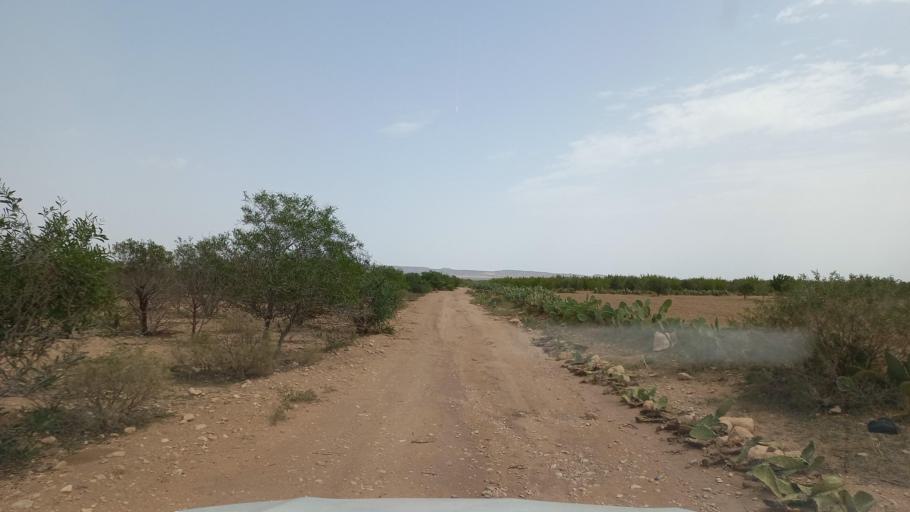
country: TN
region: Al Qasrayn
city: Kasserine
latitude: 35.2930
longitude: 9.0104
